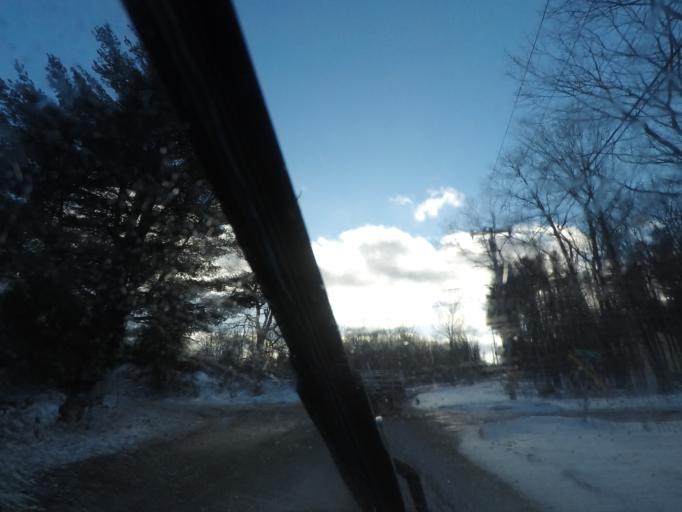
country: US
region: New York
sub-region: Rensselaer County
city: Hoosick Falls
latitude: 42.7835
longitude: -73.4078
